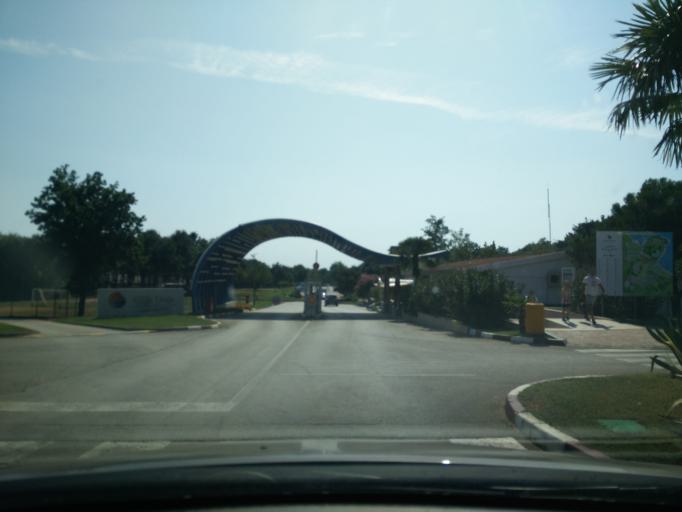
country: HR
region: Istarska
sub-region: Grad Porec
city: Porec
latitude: 45.1917
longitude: 13.5969
